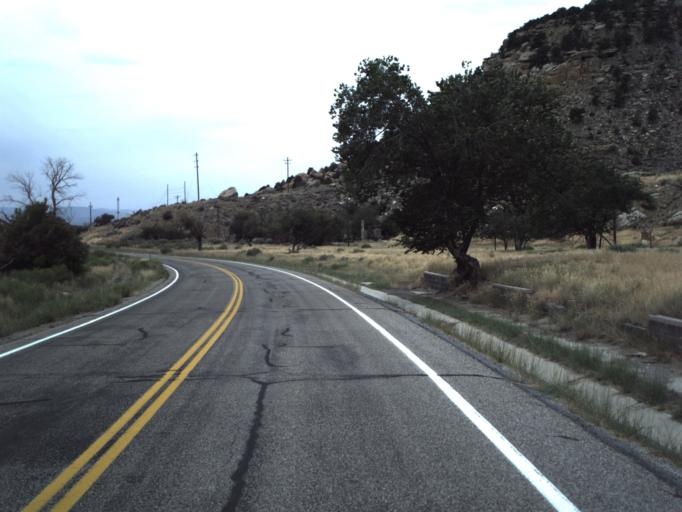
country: US
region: Utah
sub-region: Carbon County
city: East Carbon City
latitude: 39.5591
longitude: -110.3780
